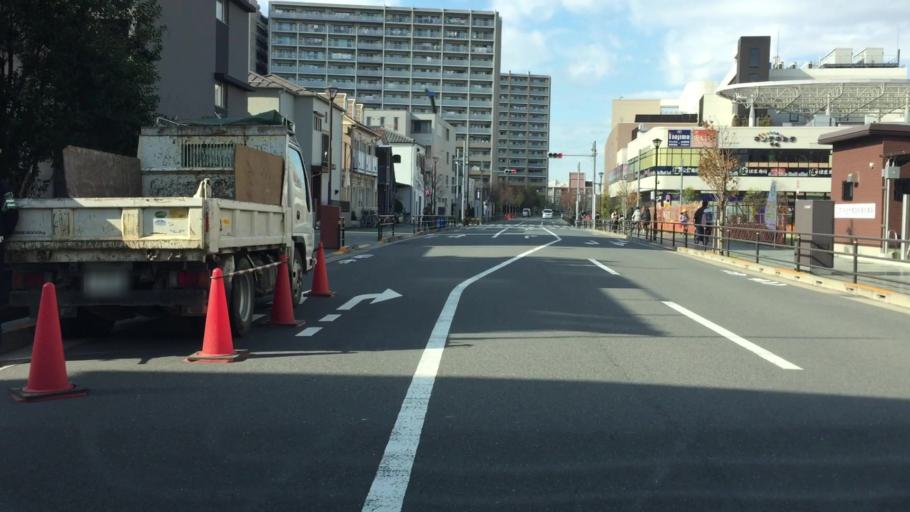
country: JP
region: Saitama
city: Soka
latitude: 35.7414
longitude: 139.7970
